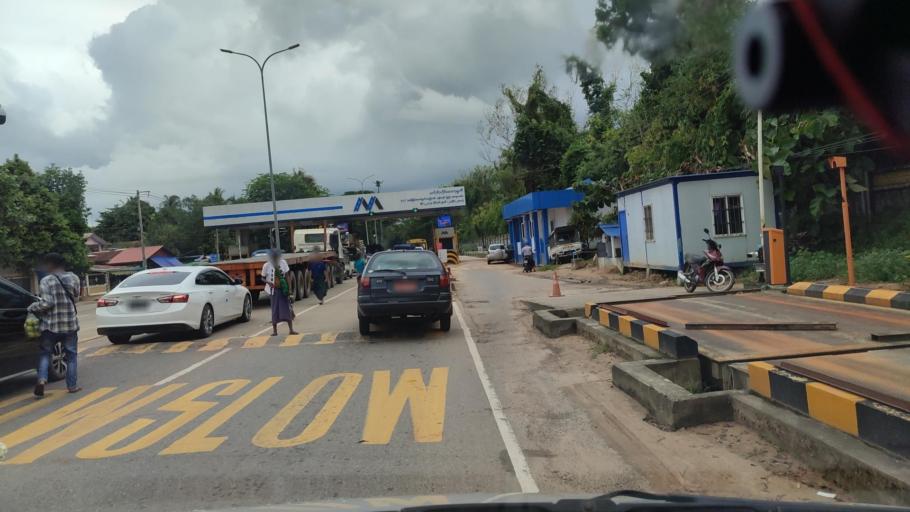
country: MM
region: Bago
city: Thanatpin
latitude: 17.0717
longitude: 96.1107
